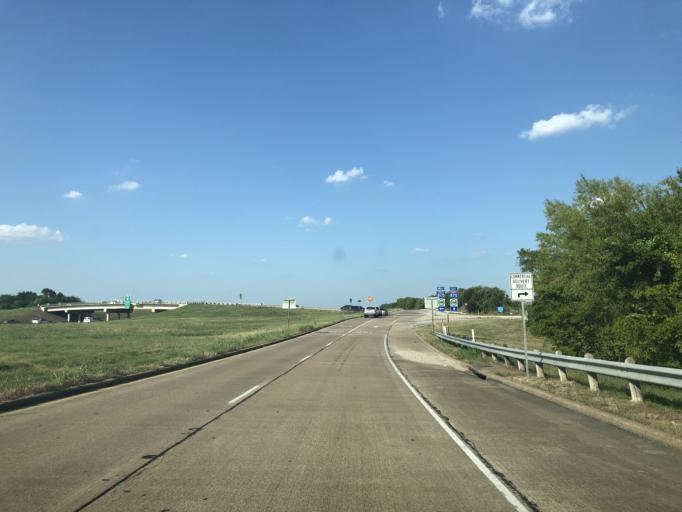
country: US
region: Texas
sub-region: Tarrant County
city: Sansom Park
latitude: 32.8277
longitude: -97.3807
